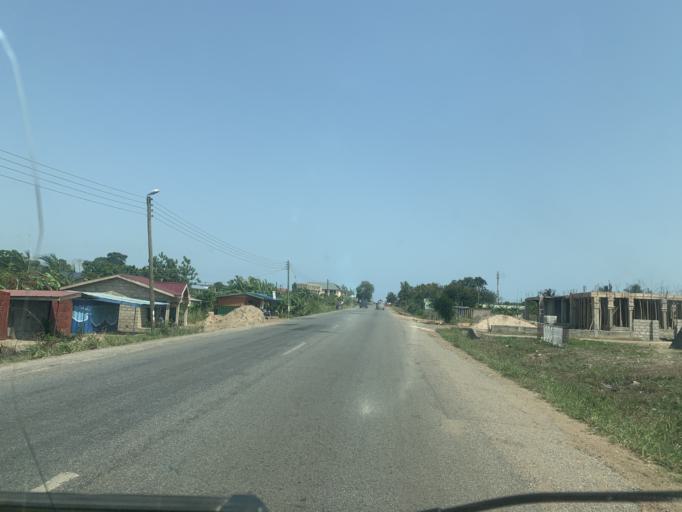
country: GH
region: Central
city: Winneba
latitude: 5.4013
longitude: -0.6512
